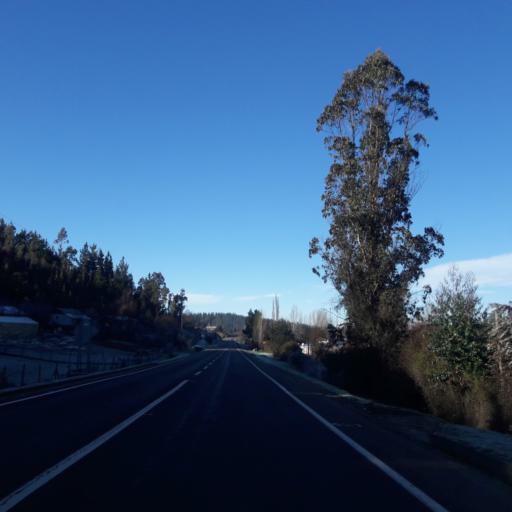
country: CL
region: Biobio
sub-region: Provincia de Biobio
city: La Laja
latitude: -37.2923
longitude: -72.9336
